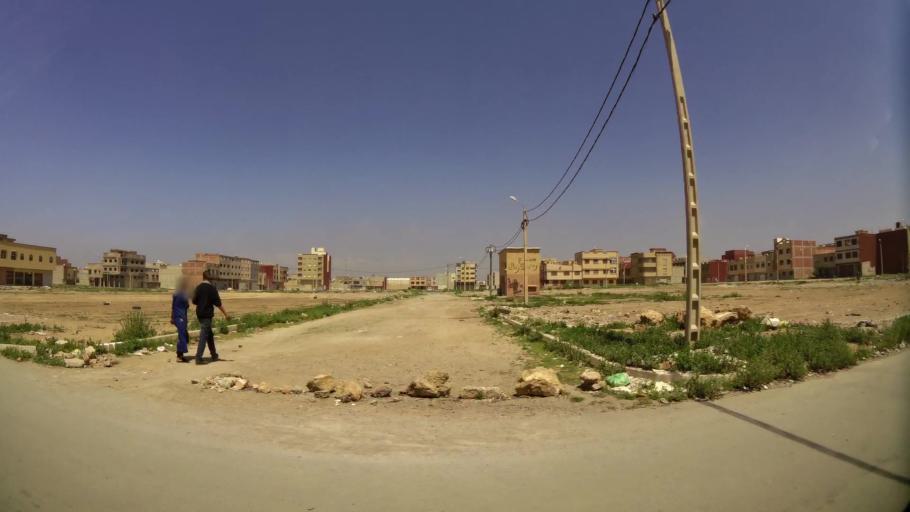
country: MA
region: Oriental
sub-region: Oujda-Angad
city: Oujda
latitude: 34.6995
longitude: -1.8880
